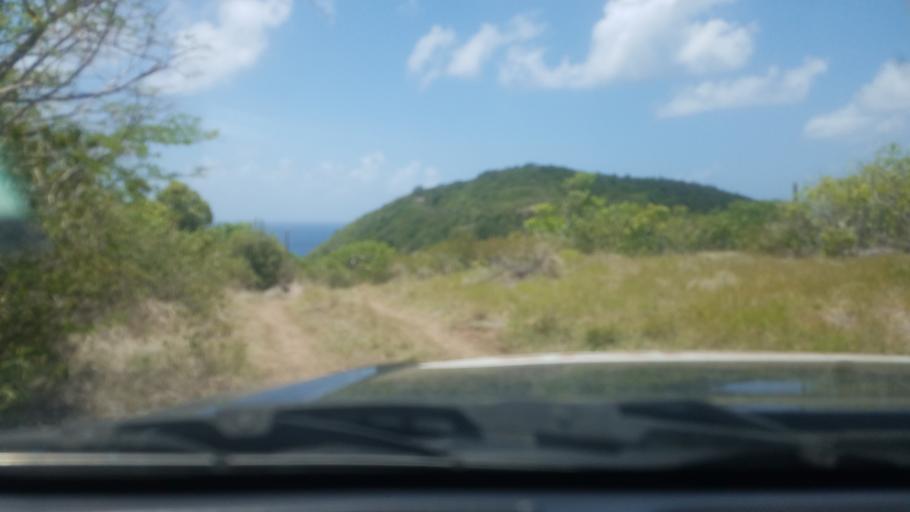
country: LC
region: Vieux-Fort
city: Vieux Fort
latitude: 13.7138
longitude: -60.9528
